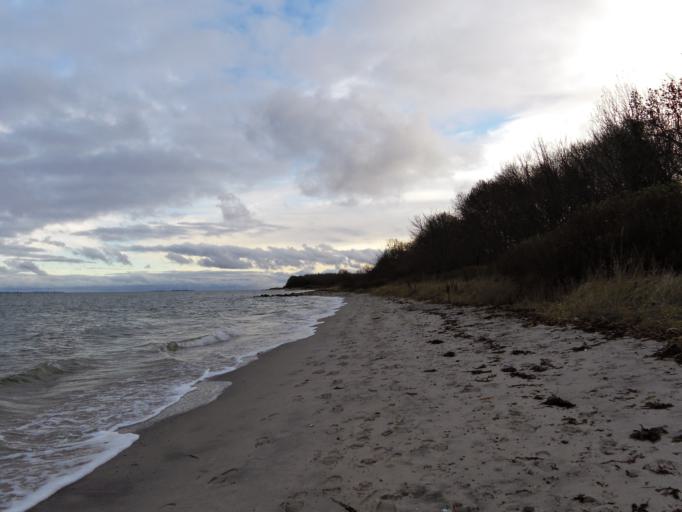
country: DK
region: Central Jutland
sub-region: Arhus Kommune
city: Beder
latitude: 56.0588
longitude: 10.2609
